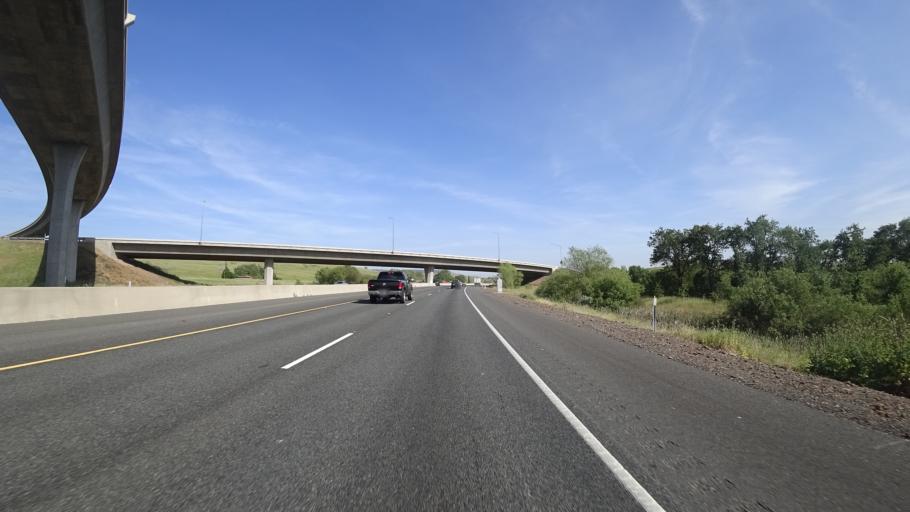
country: US
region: California
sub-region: Butte County
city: Thermalito
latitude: 39.5828
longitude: -121.6236
